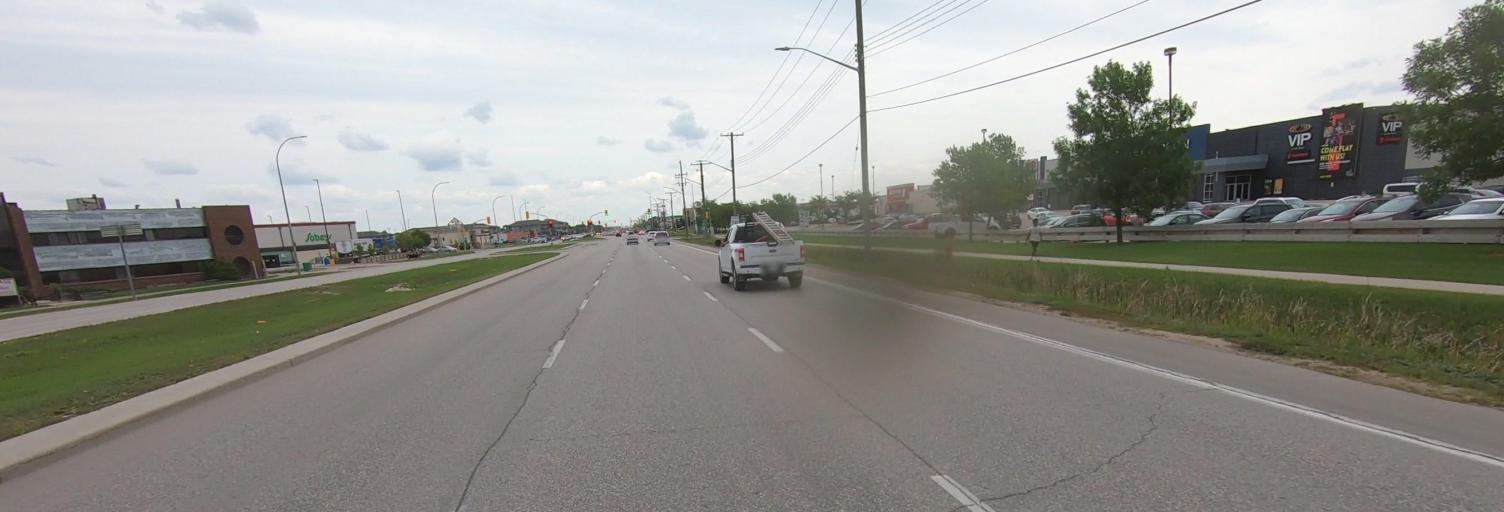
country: CA
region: Manitoba
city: Winnipeg
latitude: 49.8195
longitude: -97.2060
